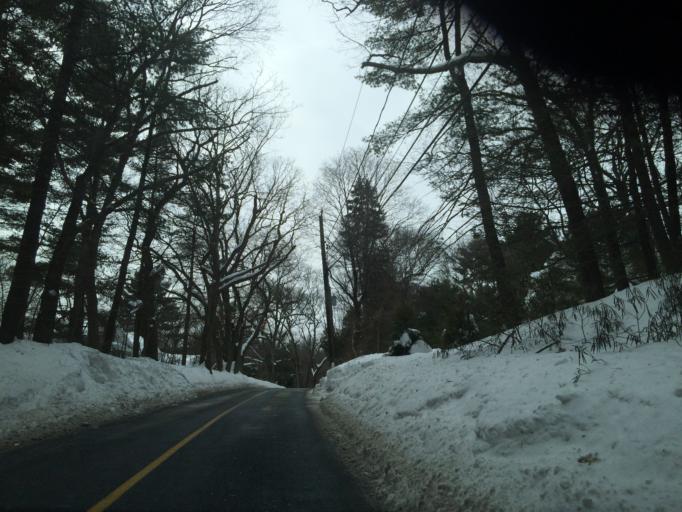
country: US
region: Massachusetts
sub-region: Middlesex County
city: Weston
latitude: 42.3478
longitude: -71.2979
